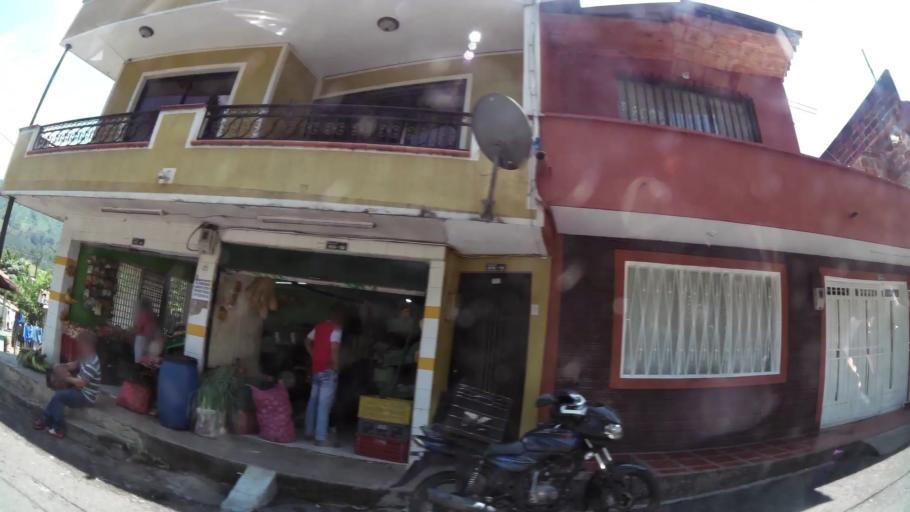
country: CO
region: Antioquia
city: La Estrella
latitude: 6.1840
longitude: -75.6435
